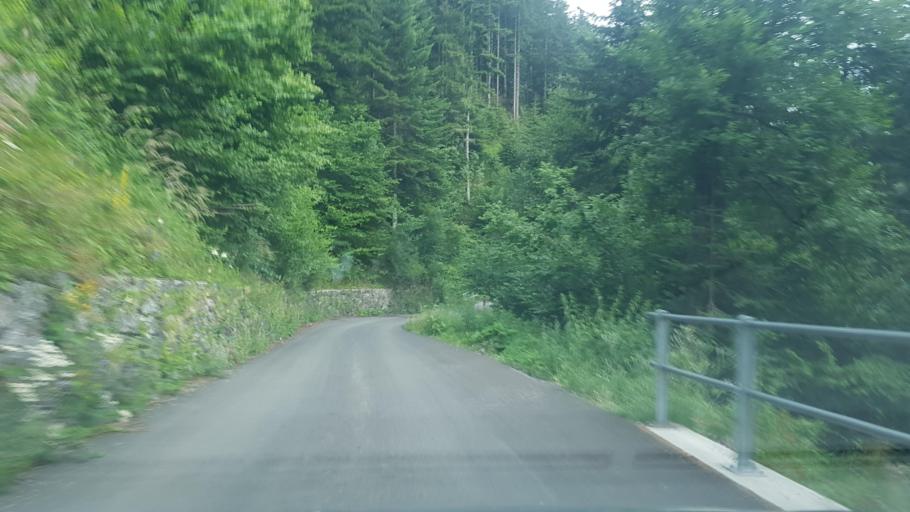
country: IT
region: Friuli Venezia Giulia
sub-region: Provincia di Udine
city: Paularo
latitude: 46.5494
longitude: 13.1231
